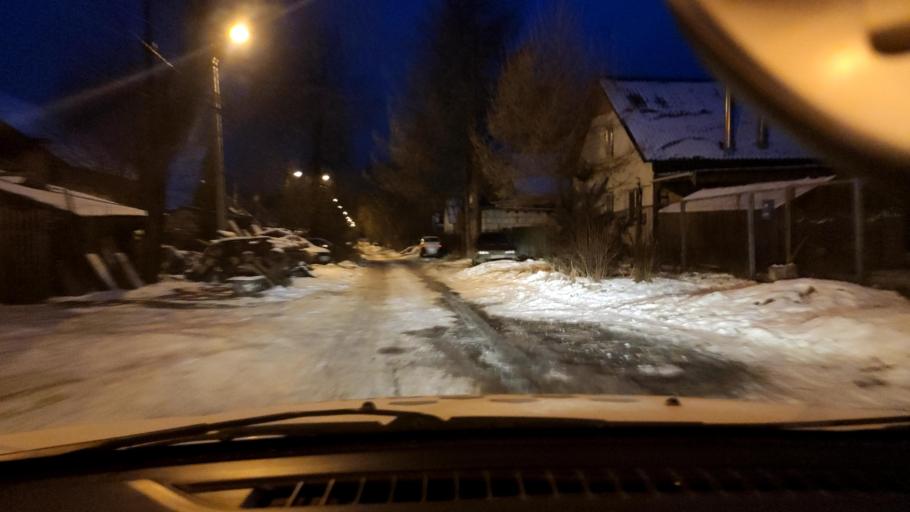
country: RU
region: Perm
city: Kondratovo
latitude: 58.0489
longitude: 56.1094
